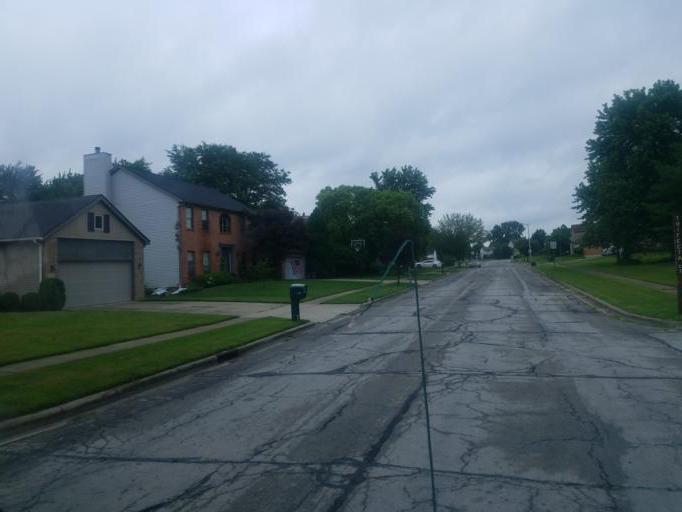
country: US
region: Ohio
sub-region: Franklin County
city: Gahanna
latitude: 40.0083
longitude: -82.8514
